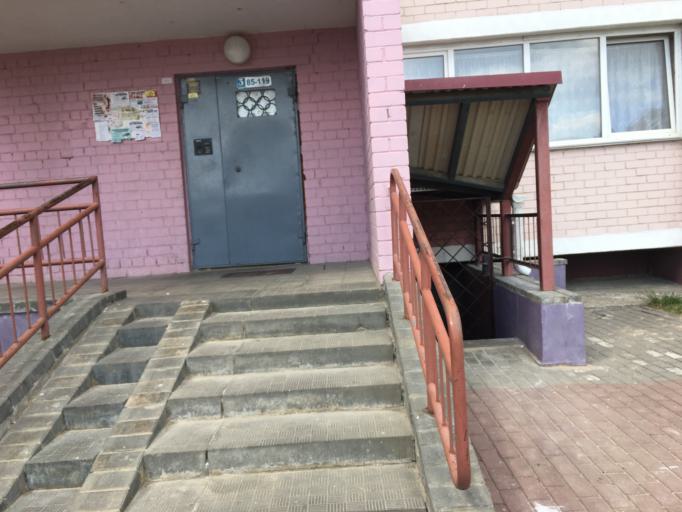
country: BY
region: Grodnenskaya
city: Hrodna
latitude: 53.7134
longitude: 23.8412
